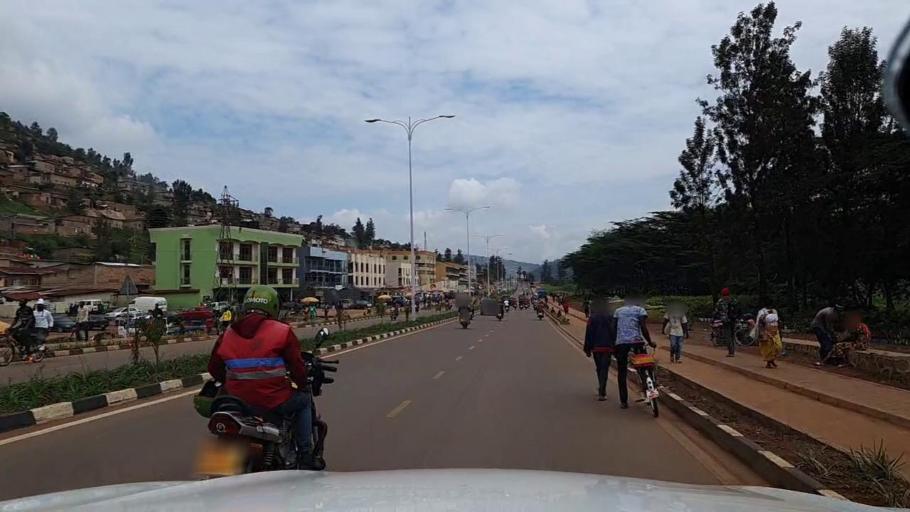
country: RW
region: Kigali
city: Kigali
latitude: -1.9386
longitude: 30.0441
